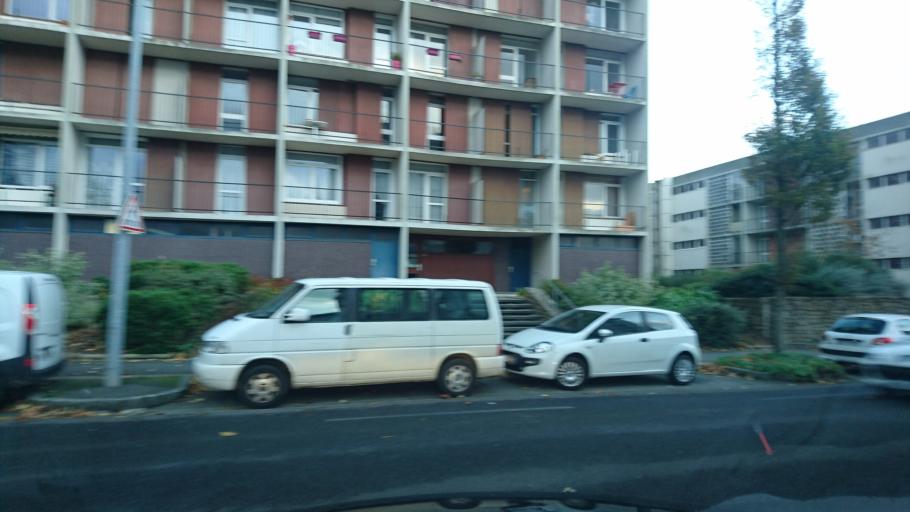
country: FR
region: Brittany
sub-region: Departement du Finistere
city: Brest
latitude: 48.3903
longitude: -4.4737
